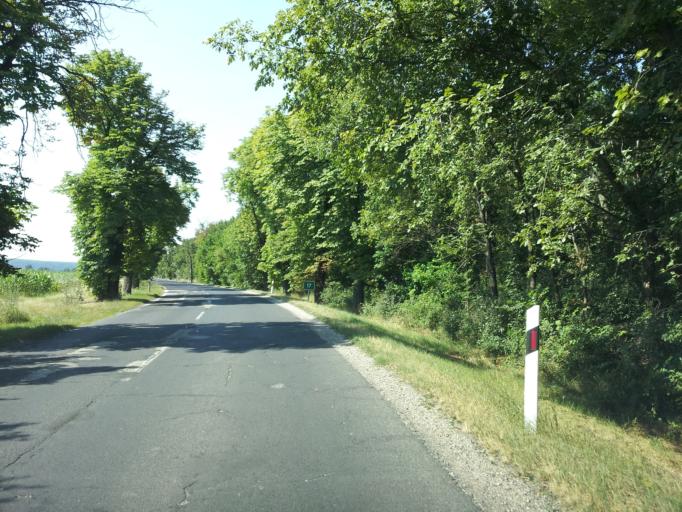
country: HU
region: Fejer
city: Lovasbereny
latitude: 47.3058
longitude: 18.5386
